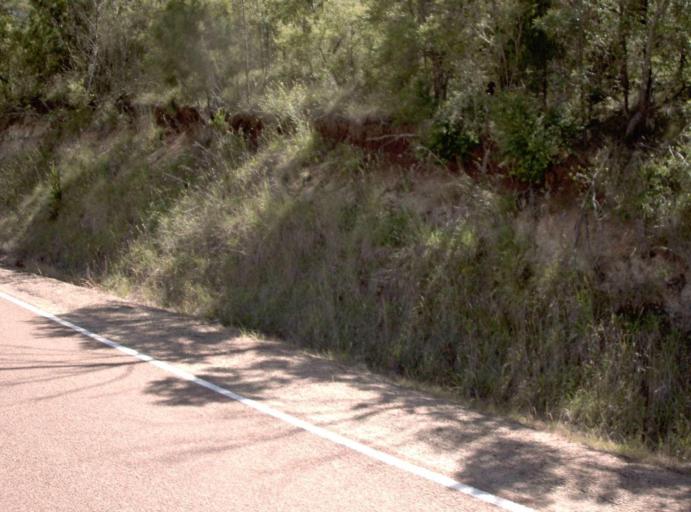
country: AU
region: Victoria
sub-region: East Gippsland
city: Lakes Entrance
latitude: -37.4790
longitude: 148.1816
